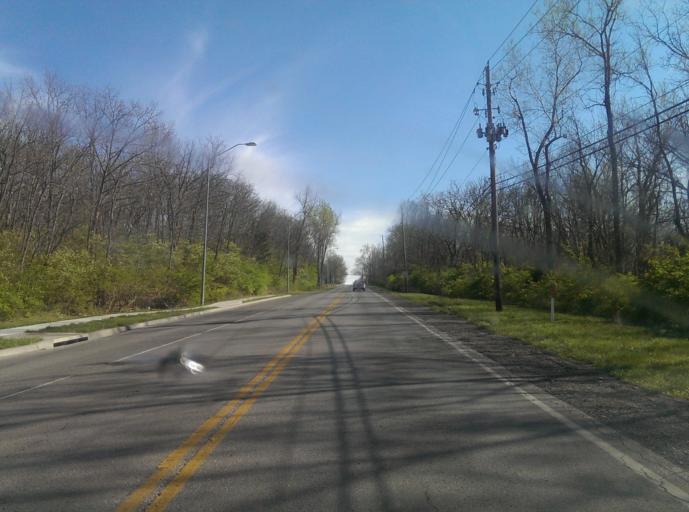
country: US
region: Missouri
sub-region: Jackson County
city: Grandview
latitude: 38.9056
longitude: -94.5942
